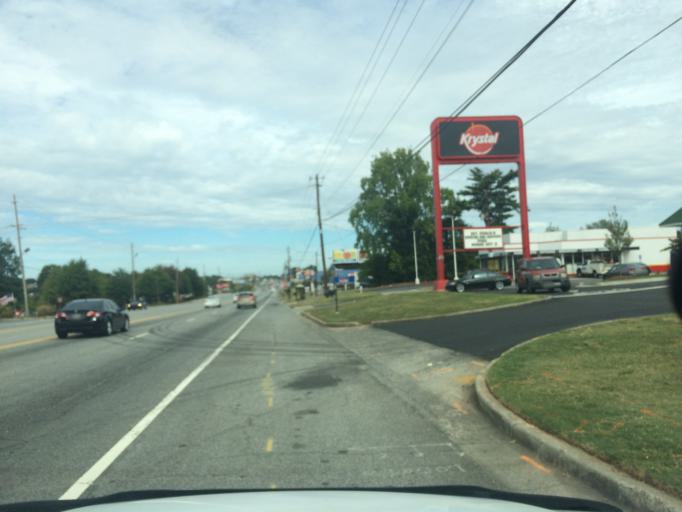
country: US
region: Georgia
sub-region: Cobb County
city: Marietta
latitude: 33.9445
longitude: -84.5171
